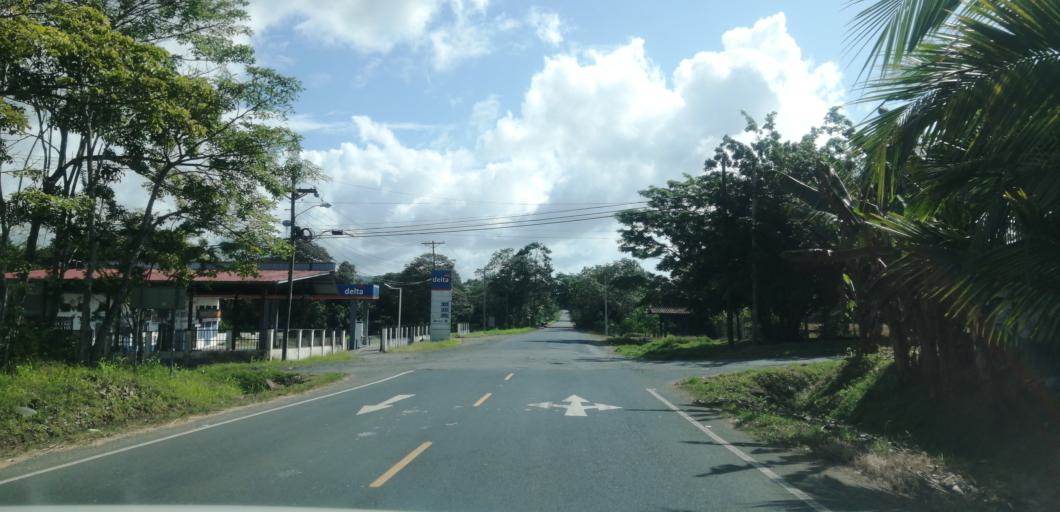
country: PA
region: Panama
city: Canita
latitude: 9.2214
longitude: -78.8896
